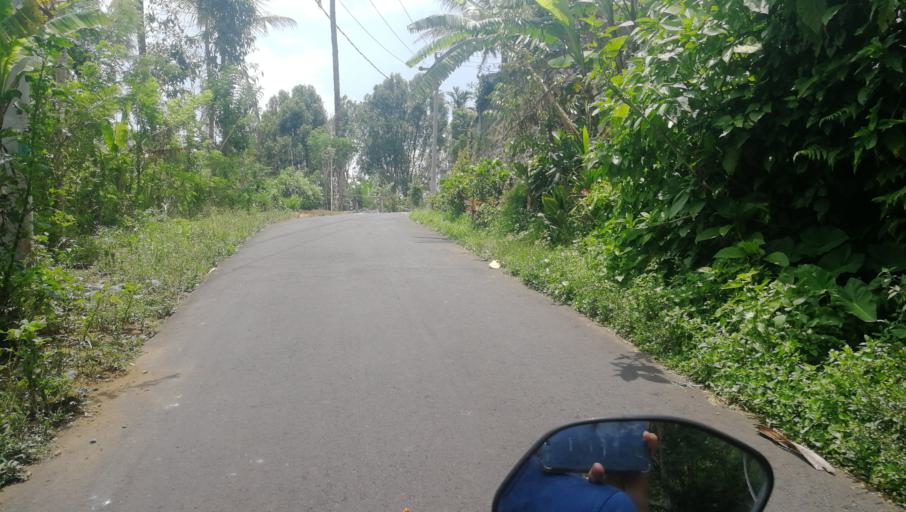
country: ID
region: Bali
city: Munduk
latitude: -8.2894
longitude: 115.0426
